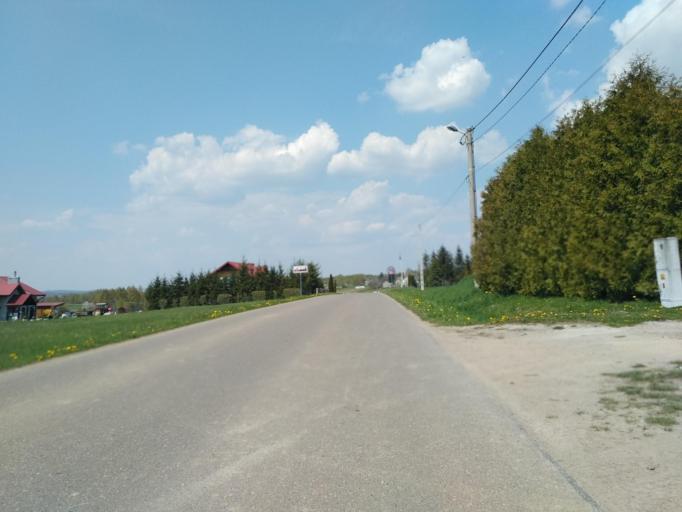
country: PL
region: Subcarpathian Voivodeship
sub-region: Powiat jasielski
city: Debowiec
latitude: 49.6895
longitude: 21.5176
